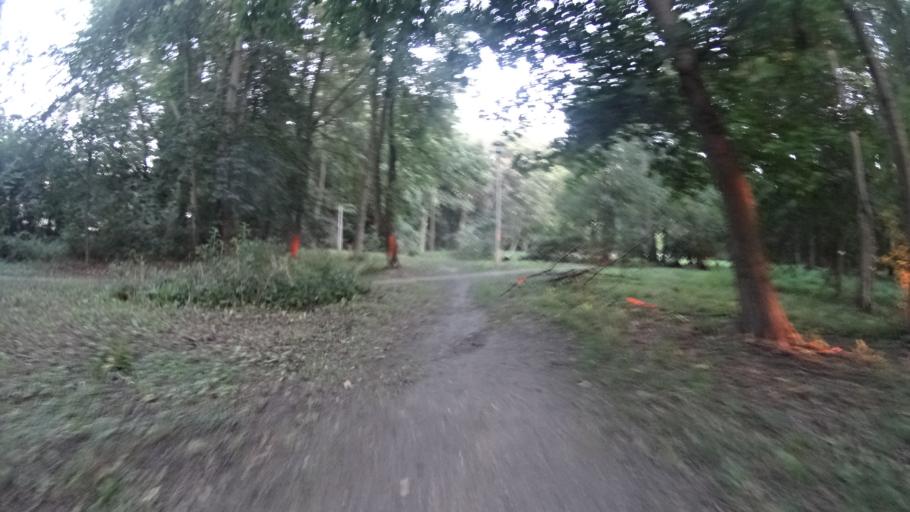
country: PL
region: Masovian Voivodeship
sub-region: Powiat warszawski zachodni
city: Ozarow Mazowiecki
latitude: 52.2180
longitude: 20.7755
